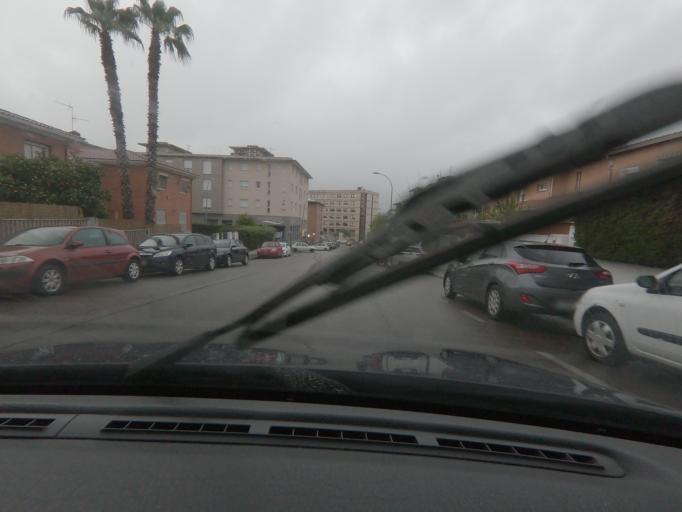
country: ES
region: Extremadura
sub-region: Provincia de Badajoz
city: Merida
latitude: 38.9108
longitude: -6.3628
